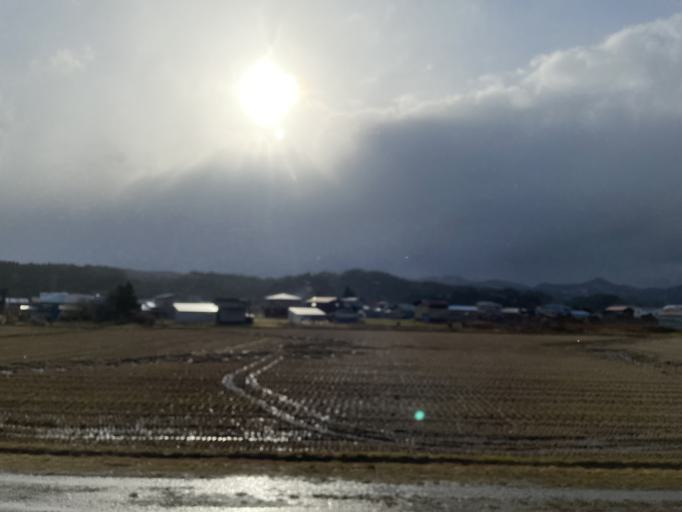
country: JP
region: Aomori
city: Aomori Shi
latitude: 41.0522
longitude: 140.5956
